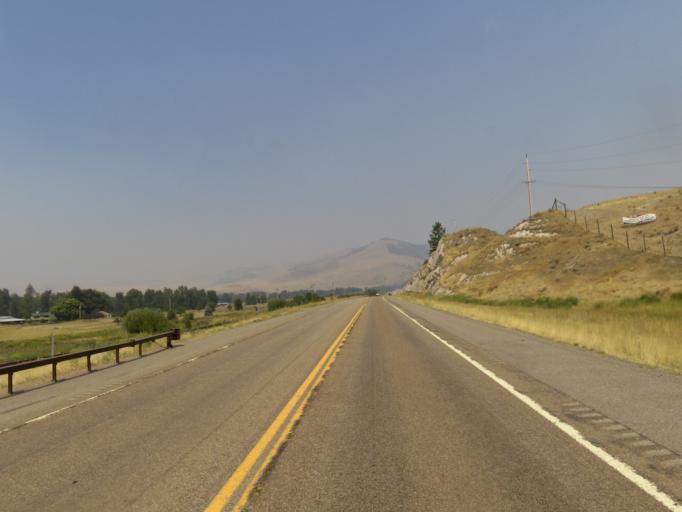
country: US
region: Montana
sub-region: Missoula County
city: Frenchtown
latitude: 47.2292
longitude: -114.1488
